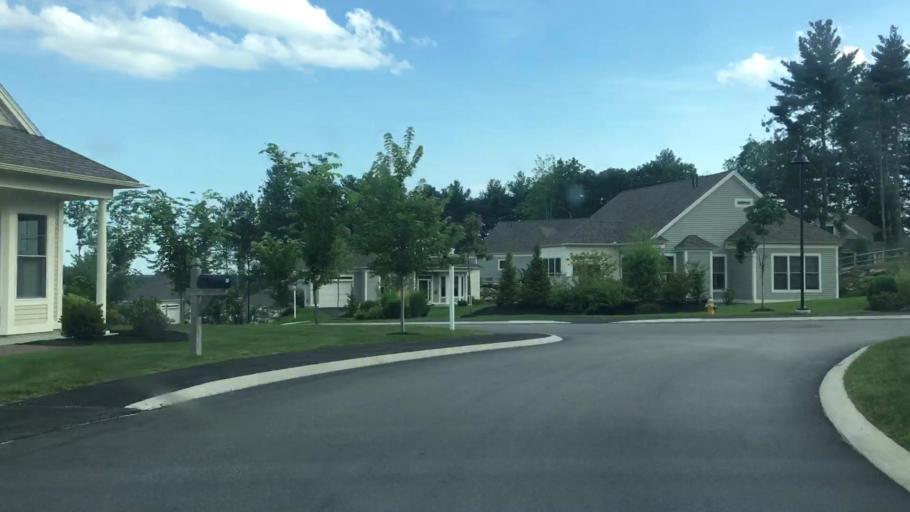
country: US
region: Maine
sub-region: Cumberland County
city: Falmouth
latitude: 43.7248
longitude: -70.2478
